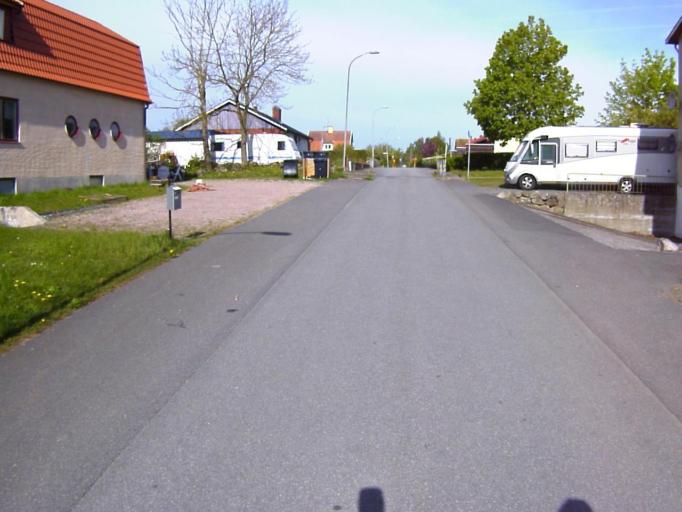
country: SE
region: Skane
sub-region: Kristianstads Kommun
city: Fjalkinge
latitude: 56.0415
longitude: 14.2769
